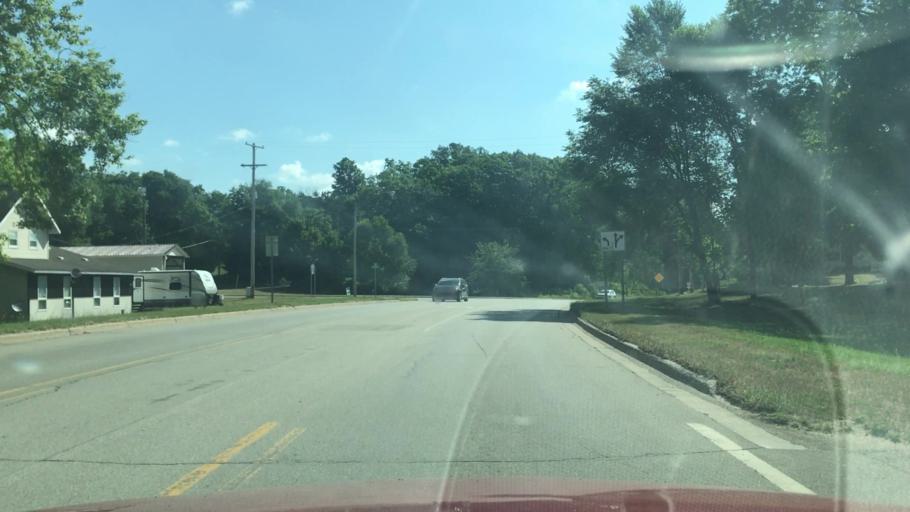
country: US
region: Michigan
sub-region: Newaygo County
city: Newaygo
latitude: 43.4242
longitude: -85.8029
